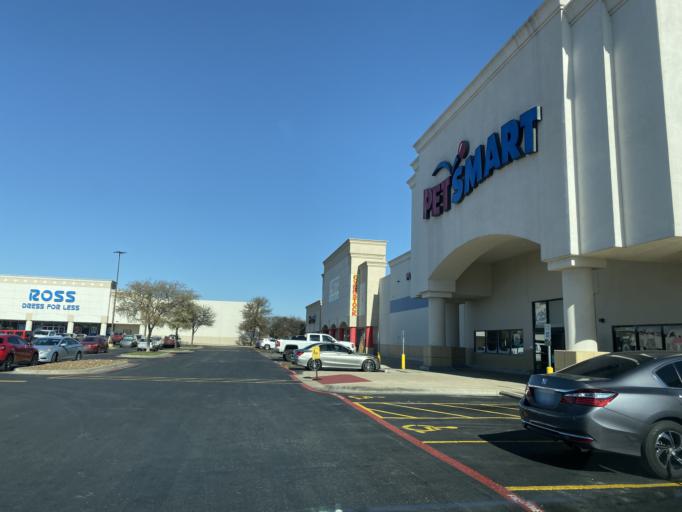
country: US
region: Texas
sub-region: Williamson County
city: Round Rock
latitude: 30.4842
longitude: -97.6708
